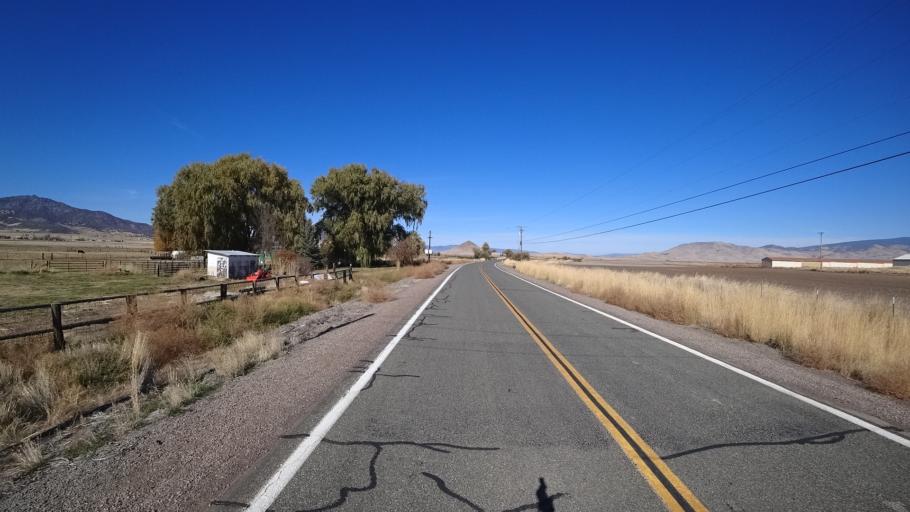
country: US
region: California
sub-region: Siskiyou County
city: Montague
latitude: 41.7812
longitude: -122.4737
